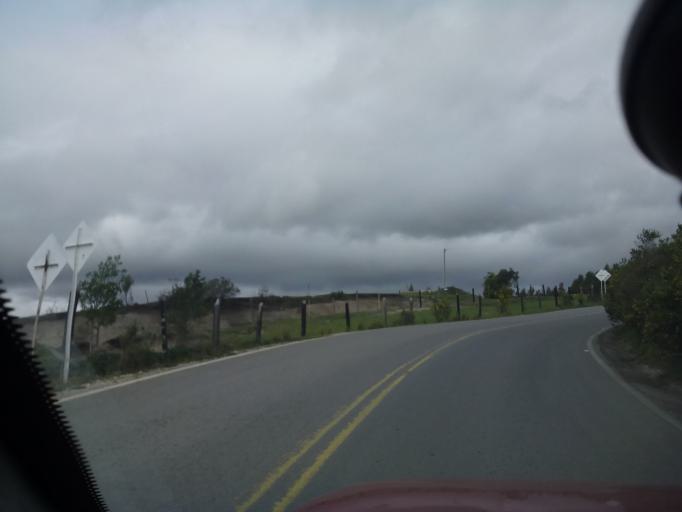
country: CO
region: Boyaca
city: Combita
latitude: 5.6362
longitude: -73.3408
